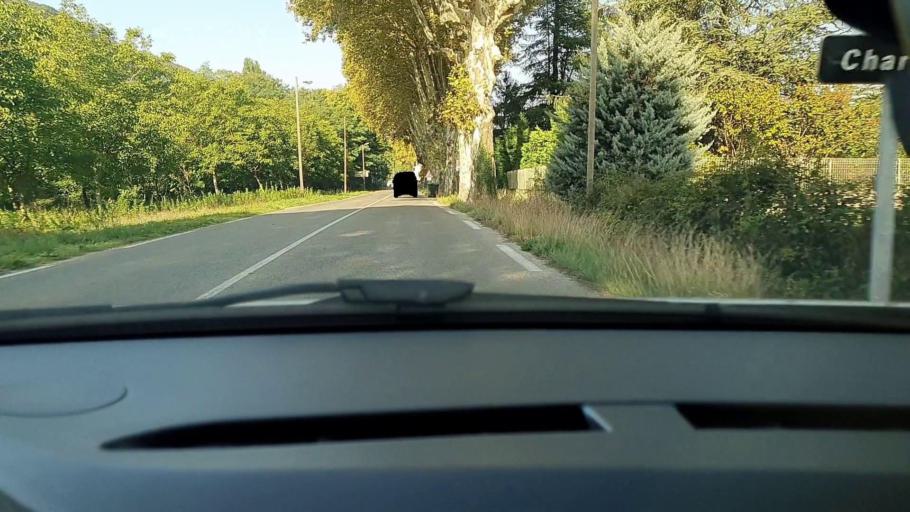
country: FR
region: Languedoc-Roussillon
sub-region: Departement du Gard
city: Besseges
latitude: 44.2841
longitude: 4.1170
